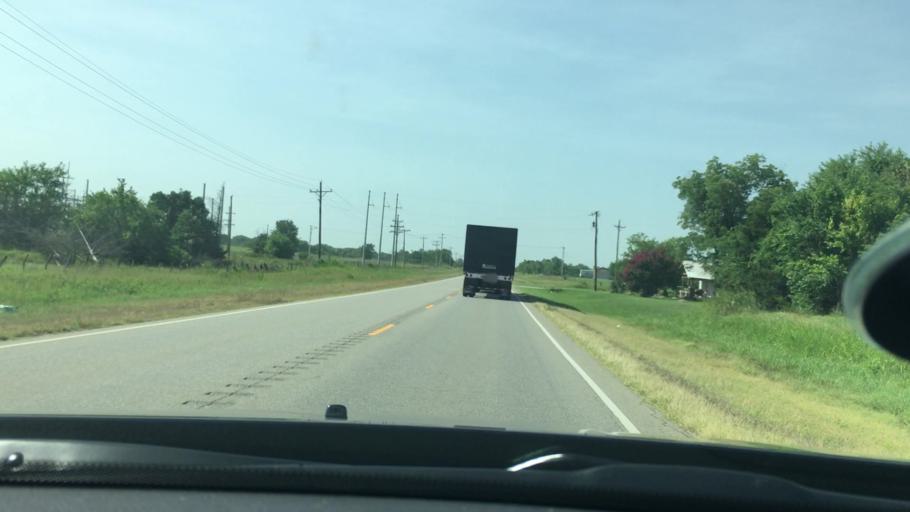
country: US
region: Oklahoma
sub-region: Coal County
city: Coalgate
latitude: 34.4872
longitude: -96.2187
